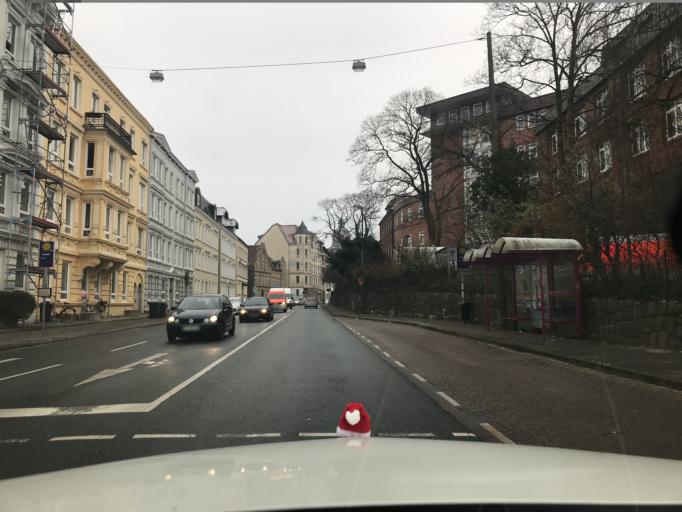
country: DE
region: Schleswig-Holstein
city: Flensburg
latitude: 54.7910
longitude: 9.4257
